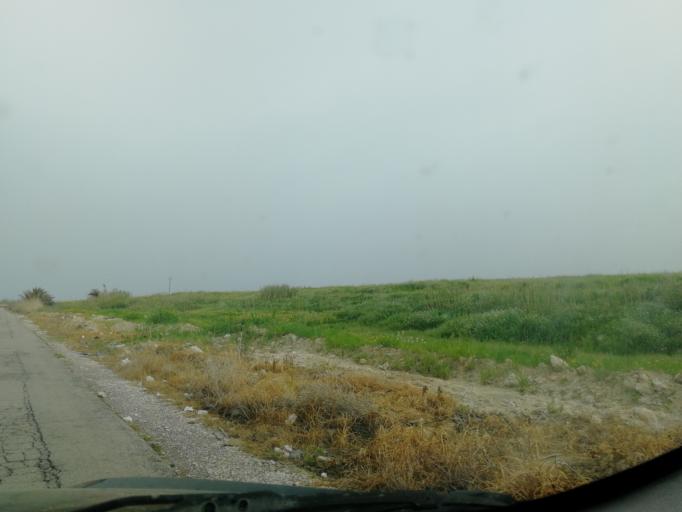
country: IT
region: Apulia
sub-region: Provincia di Barletta - Andria - Trani
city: Barletta
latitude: 41.3180
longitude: 16.3055
